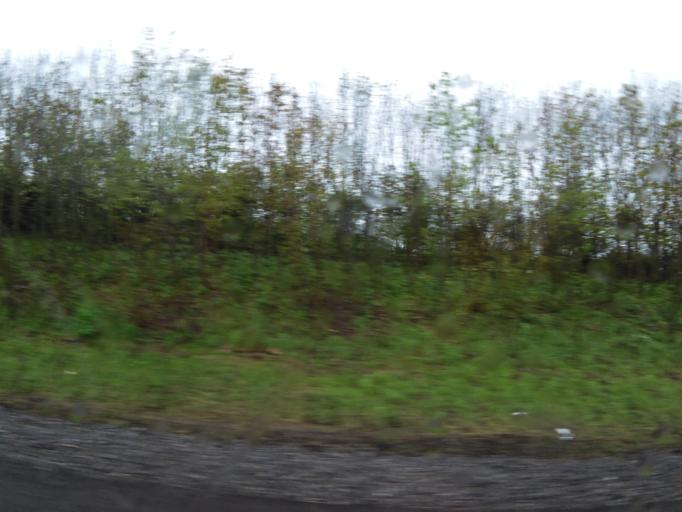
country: IE
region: Leinster
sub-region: Kildare
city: Maynooth
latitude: 53.3708
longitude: -6.6088
